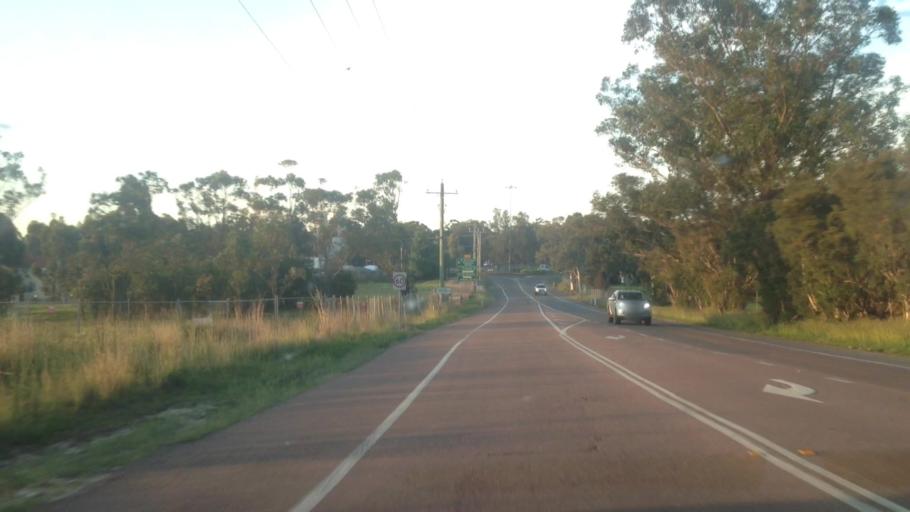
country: AU
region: New South Wales
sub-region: Lake Macquarie Shire
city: Dora Creek
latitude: -33.1155
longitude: 151.4782
